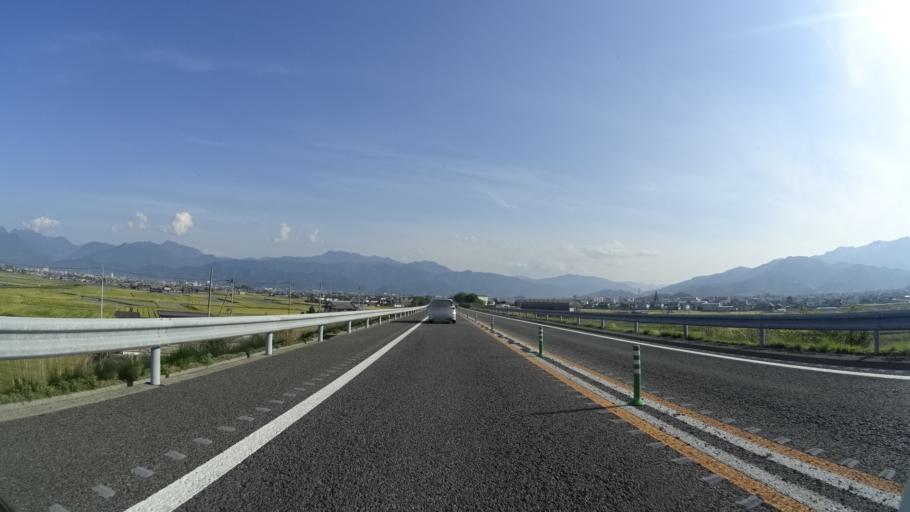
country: JP
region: Ehime
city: Saijo
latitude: 33.9470
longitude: 133.0691
